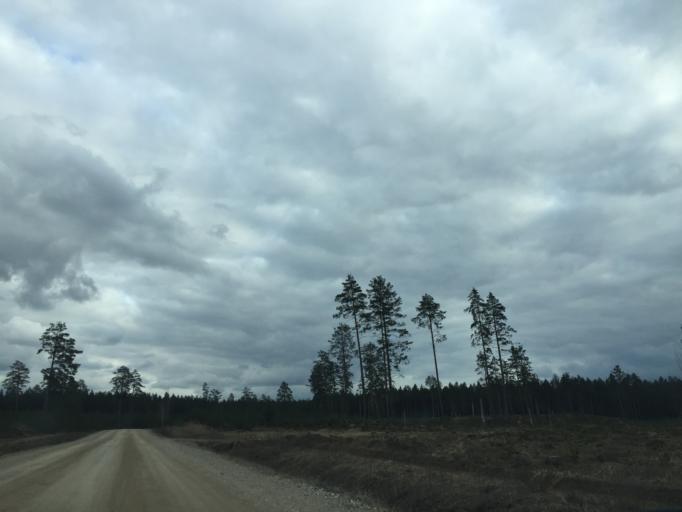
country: LV
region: Jaunjelgava
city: Jaunjelgava
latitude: 56.5816
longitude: 25.0072
